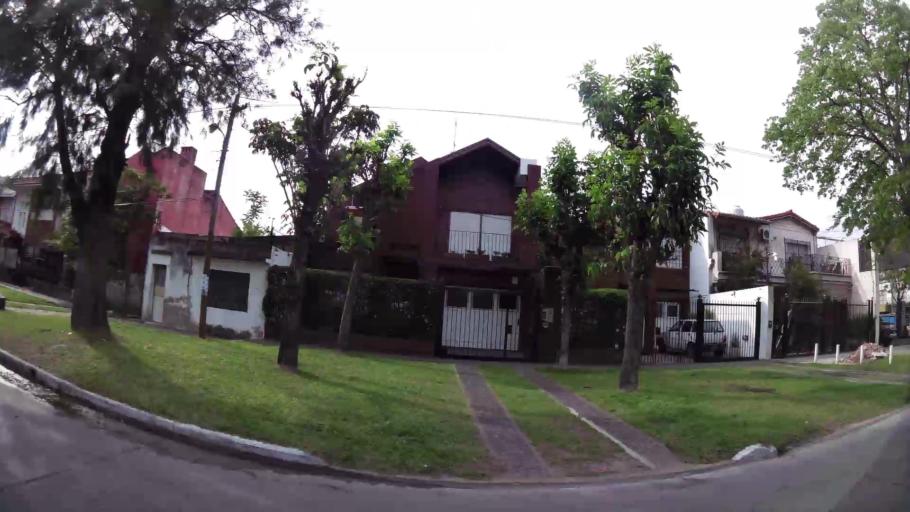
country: AR
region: Buenos Aires
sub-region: Partido de Quilmes
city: Quilmes
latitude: -34.7167
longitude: -58.2471
